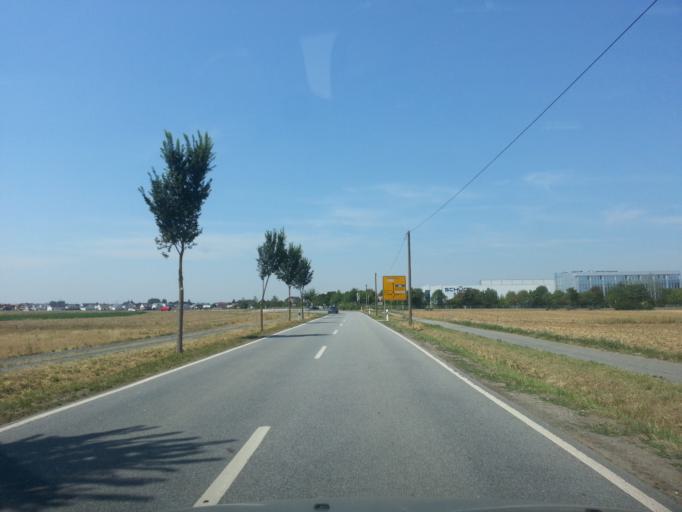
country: DE
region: Hesse
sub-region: Regierungsbezirk Darmstadt
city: Gross-Rohrheim
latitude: 49.7157
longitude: 8.4953
